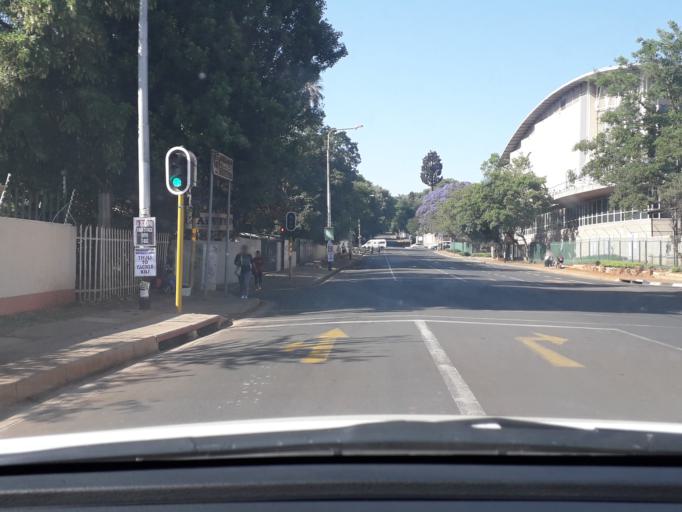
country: ZA
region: Gauteng
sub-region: City of Johannesburg Metropolitan Municipality
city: Johannesburg
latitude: -26.1820
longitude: 28.0067
